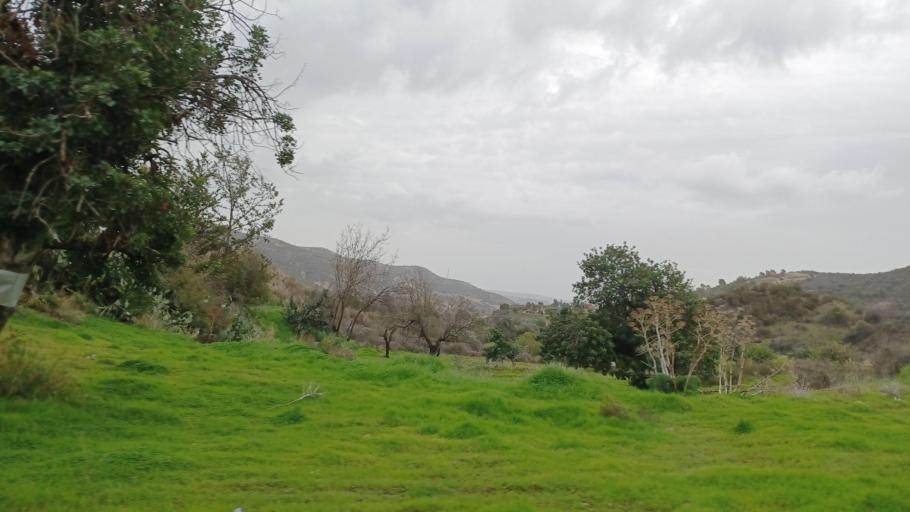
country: CY
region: Limassol
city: Pyrgos
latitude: 34.7759
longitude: 33.2545
